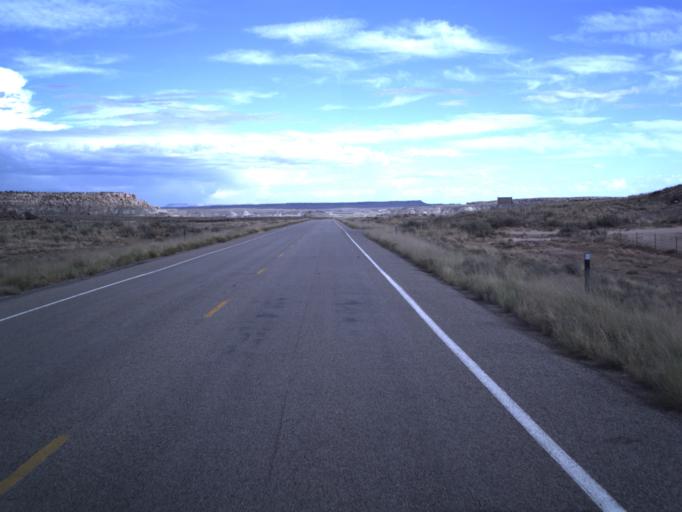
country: US
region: Colorado
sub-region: Montezuma County
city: Towaoc
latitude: 37.1686
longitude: -109.0842
